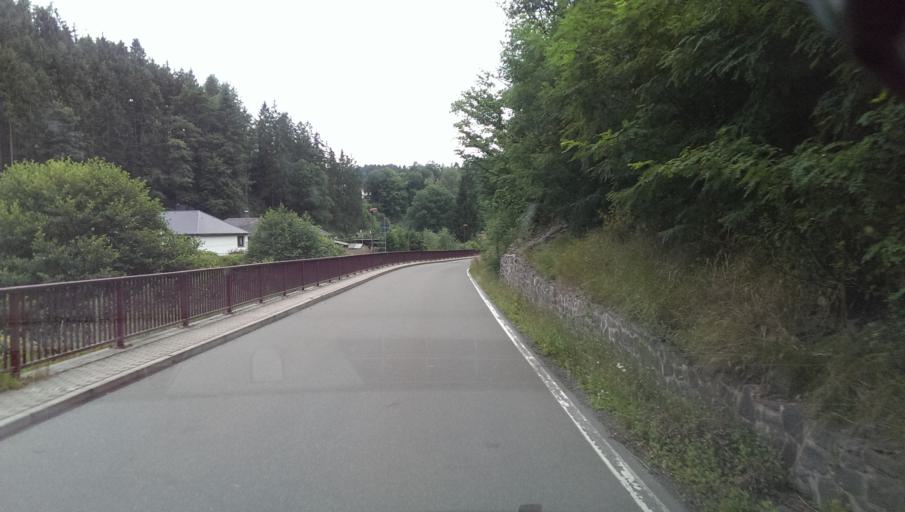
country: DE
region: Thuringia
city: Paska
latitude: 50.6083
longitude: 11.6545
